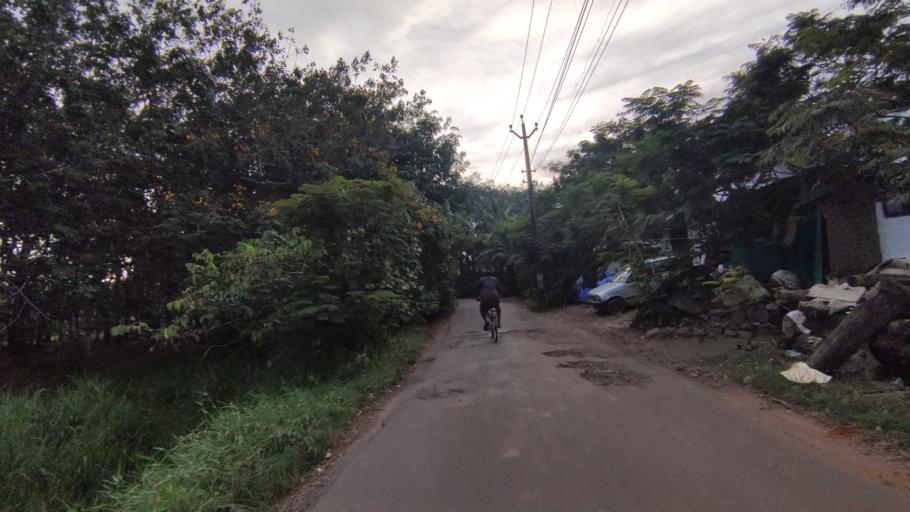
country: IN
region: Kerala
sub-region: Kottayam
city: Kottayam
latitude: 9.6345
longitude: 76.4984
